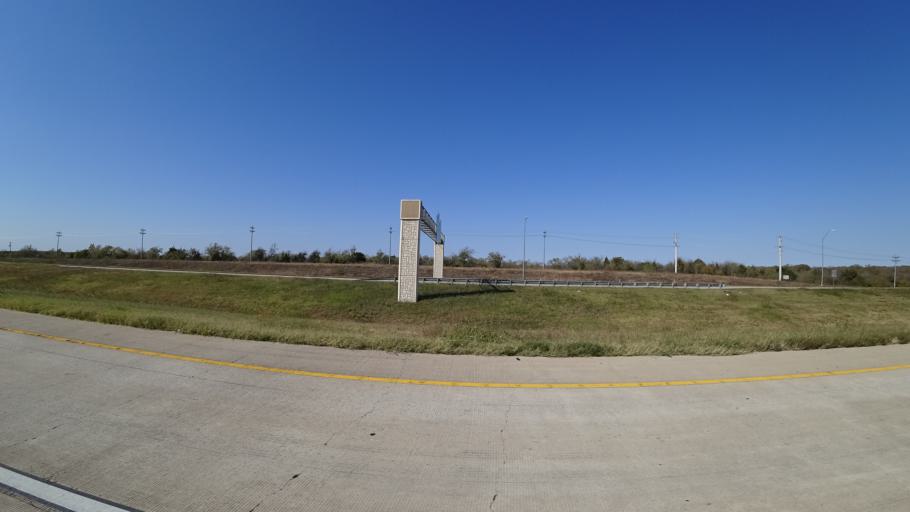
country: US
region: Texas
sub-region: Travis County
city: Manor
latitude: 30.3567
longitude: -97.5891
